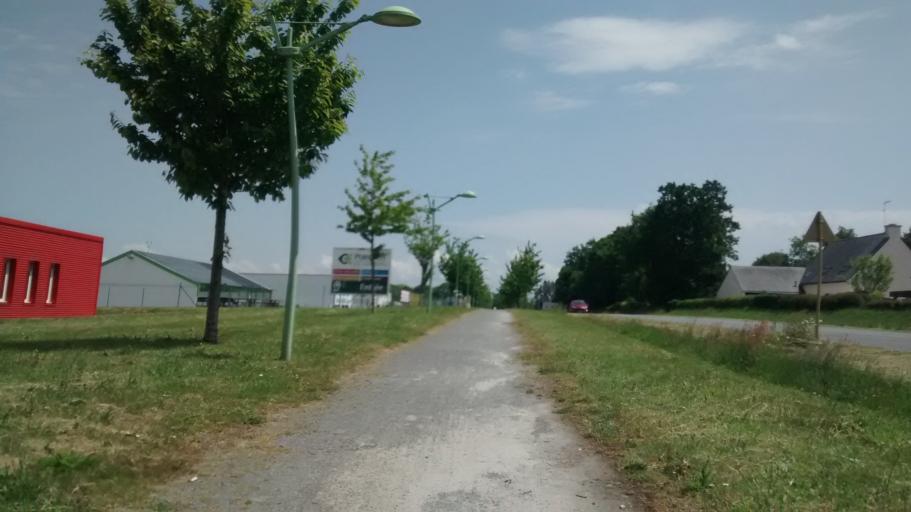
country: FR
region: Brittany
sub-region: Departement du Morbihan
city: Questembert
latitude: 47.6682
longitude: -2.4467
